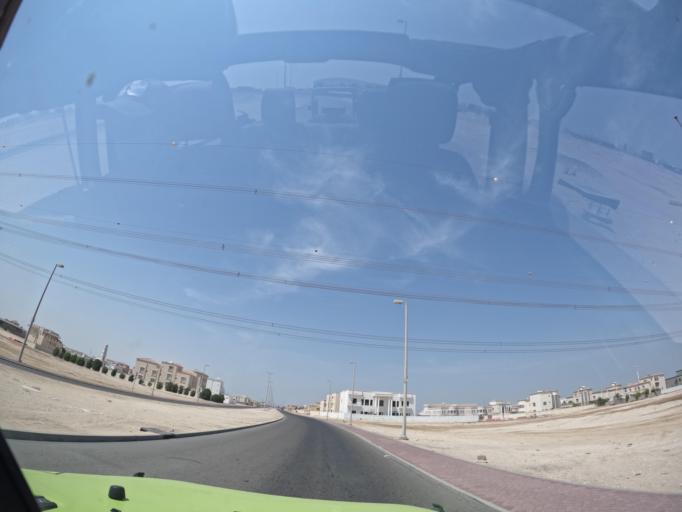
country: AE
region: Abu Dhabi
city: Abu Dhabi
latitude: 24.3168
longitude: 54.5800
